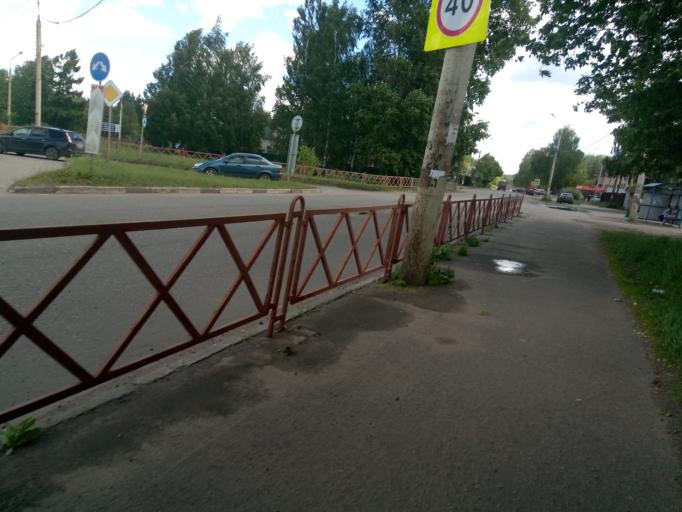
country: RU
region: Jaroslavl
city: Yaroslavl
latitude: 57.6593
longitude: 39.9589
